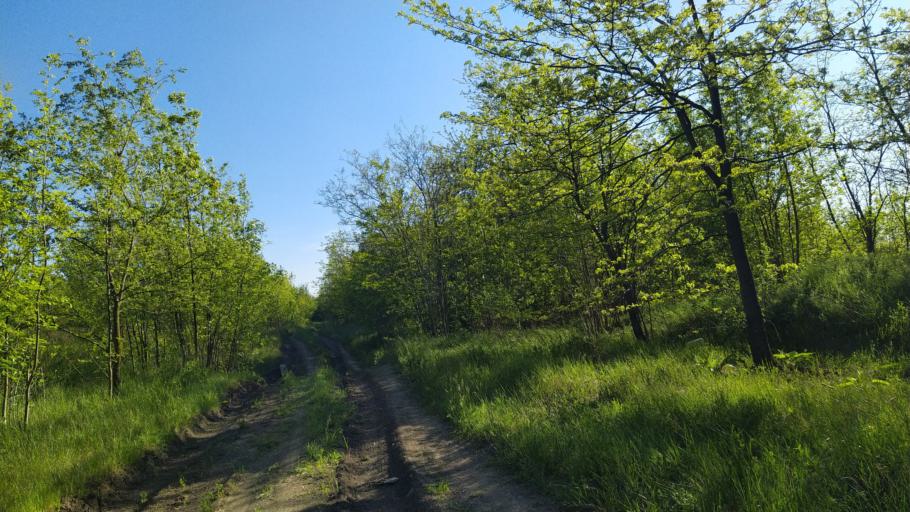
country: RU
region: Rostov
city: Bataysk
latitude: 47.0781
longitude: 39.7185
